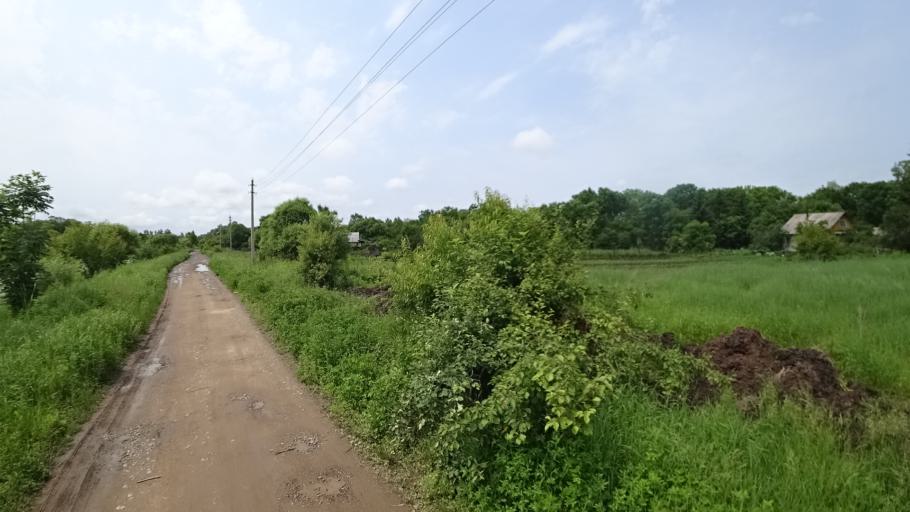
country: RU
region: Primorskiy
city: Novosysoyevka
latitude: 44.2521
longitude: 133.3741
